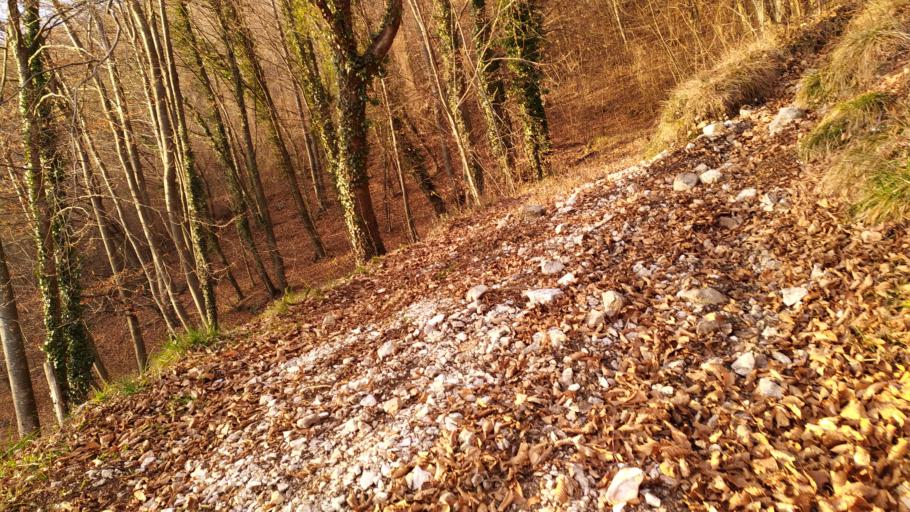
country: IT
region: Veneto
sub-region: Provincia di Vicenza
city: Velo d'Astico
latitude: 45.7650
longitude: 11.3667
